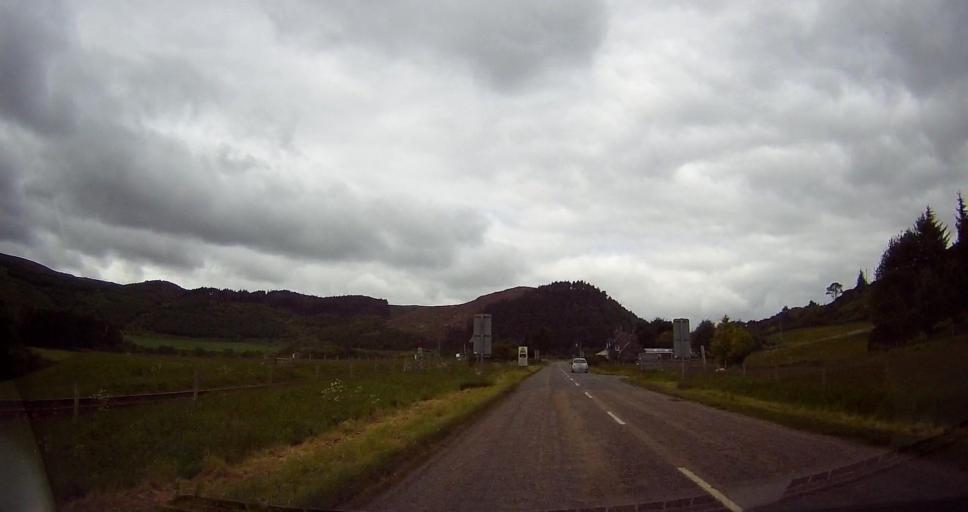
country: GB
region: Scotland
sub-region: Highland
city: Dornoch
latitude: 57.9919
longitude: -4.1662
